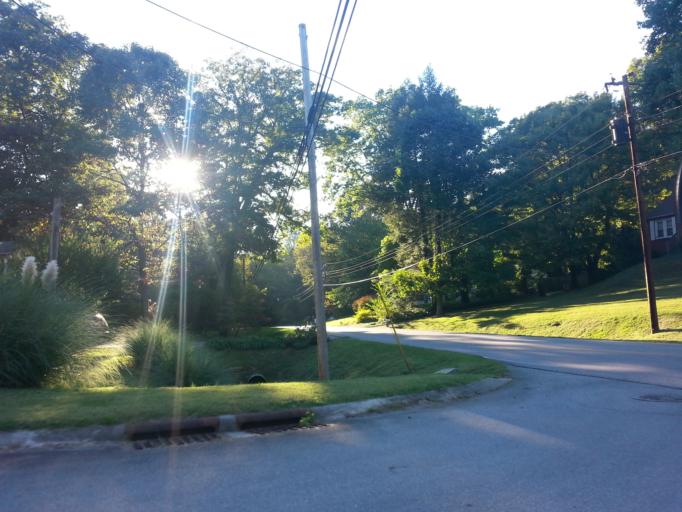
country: US
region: Tennessee
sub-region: Blount County
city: Eagleton Village
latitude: 35.7872
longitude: -83.9314
